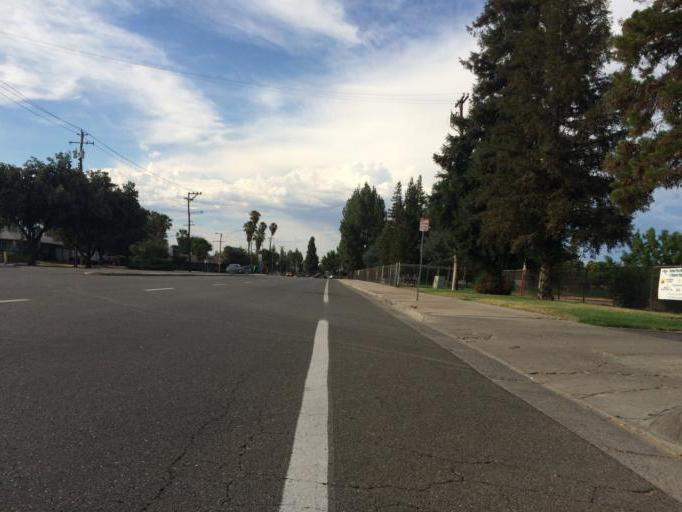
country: US
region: California
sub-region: Fresno County
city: Clovis
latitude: 36.8189
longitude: -119.7722
